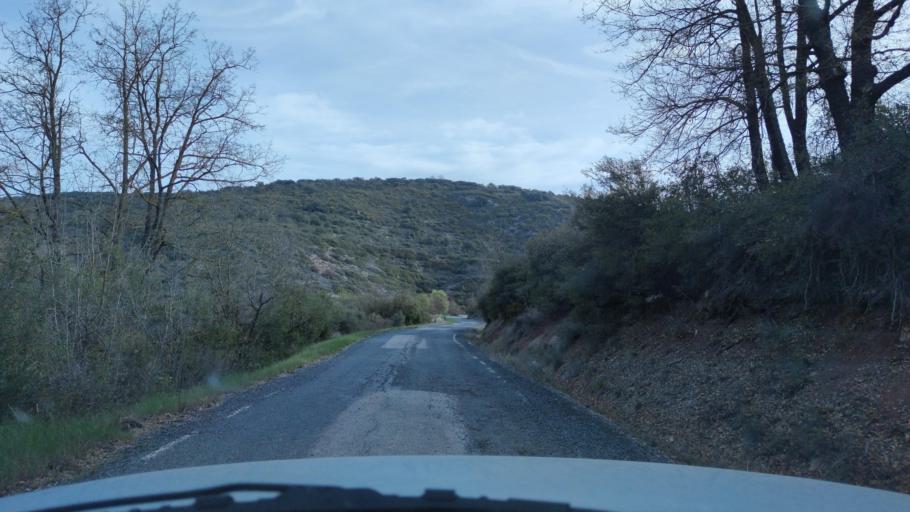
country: ES
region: Catalonia
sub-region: Provincia de Lleida
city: Os de Balaguer
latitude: 41.8885
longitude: 0.7936
